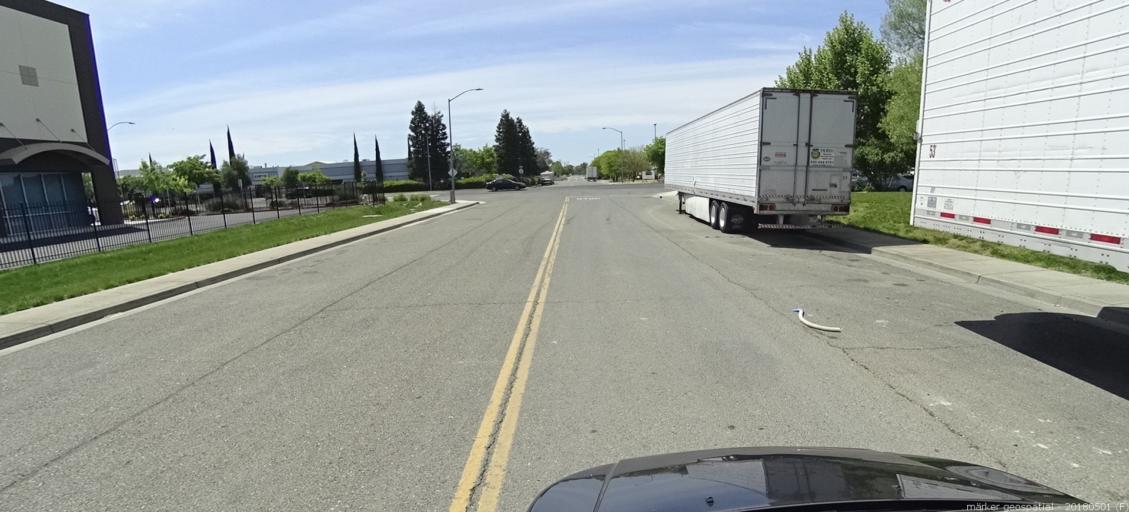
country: US
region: California
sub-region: Sacramento County
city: Rio Linda
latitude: 38.6655
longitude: -121.4283
